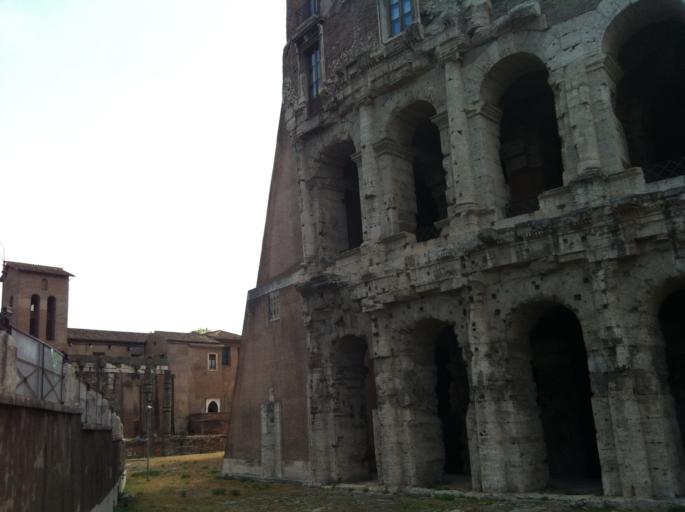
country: VA
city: Vatican City
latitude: 41.8921
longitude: 12.4801
